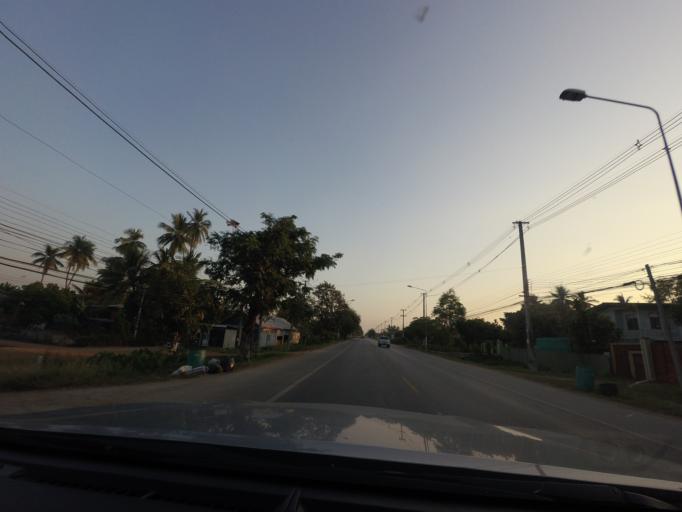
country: TH
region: Sukhothai
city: Si Samrong
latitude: 17.1364
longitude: 99.8500
